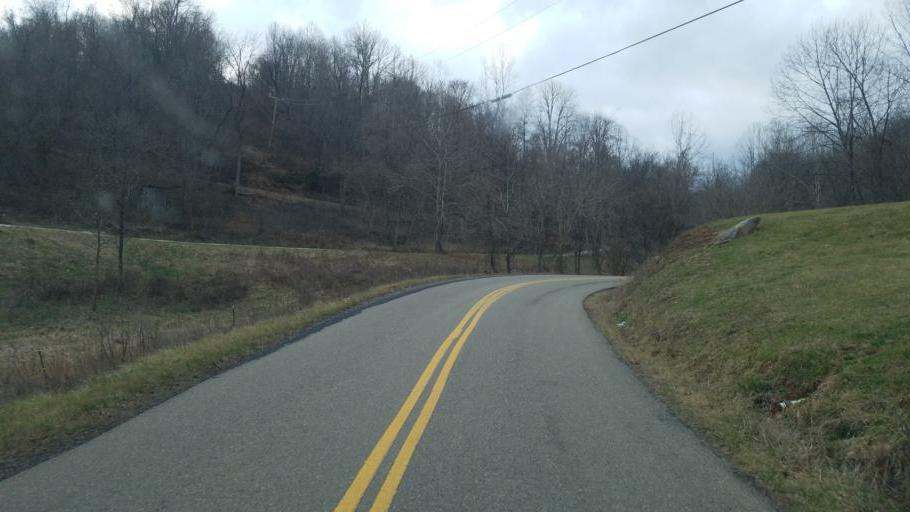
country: US
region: Ohio
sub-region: Gallia County
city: Gallipolis
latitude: 38.7176
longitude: -82.3321
